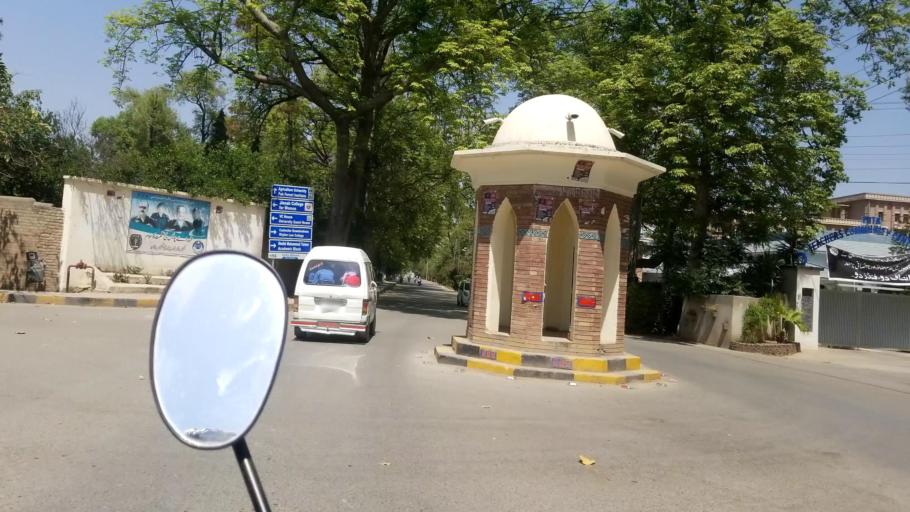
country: PK
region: Khyber Pakhtunkhwa
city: Peshawar
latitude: 34.0071
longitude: 71.4866
